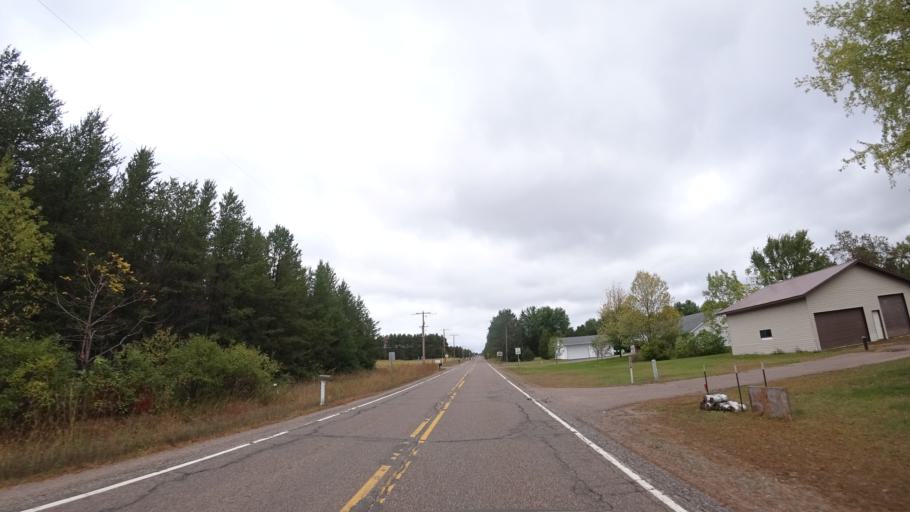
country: US
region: Wisconsin
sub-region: Chippewa County
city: Lake Wissota
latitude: 44.9545
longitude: -91.2678
